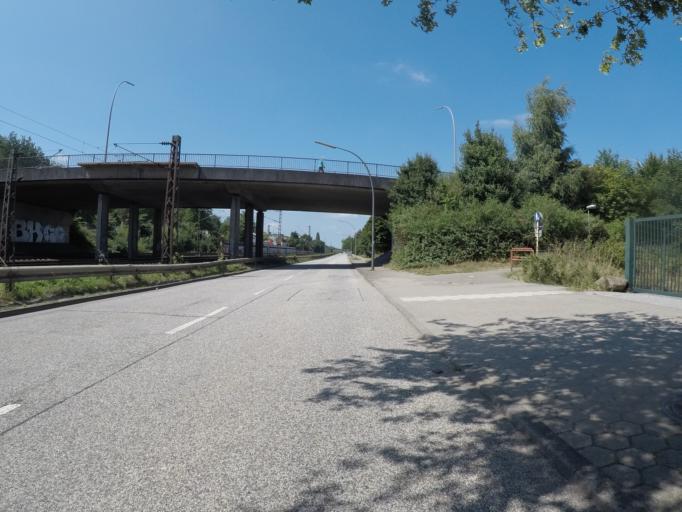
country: DE
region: Hamburg
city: Harburg
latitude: 53.4717
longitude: 9.9391
